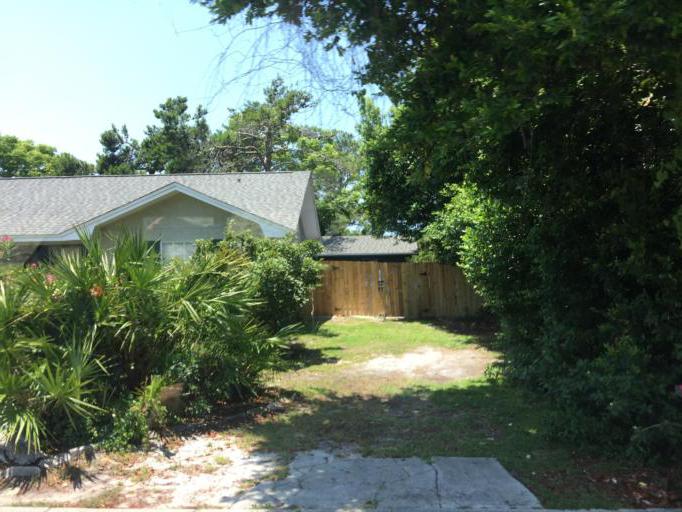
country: US
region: Florida
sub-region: Bay County
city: Panama City Beach
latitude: 30.2105
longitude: -85.8578
